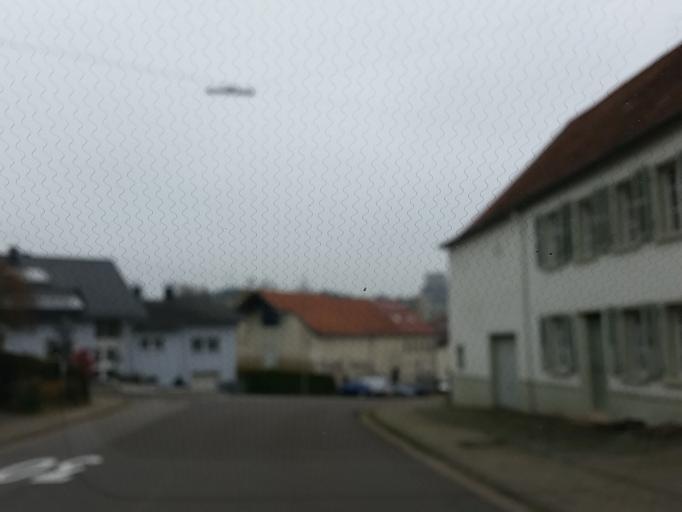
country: DE
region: Saarland
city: Lebach
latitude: 49.4131
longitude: 6.9105
